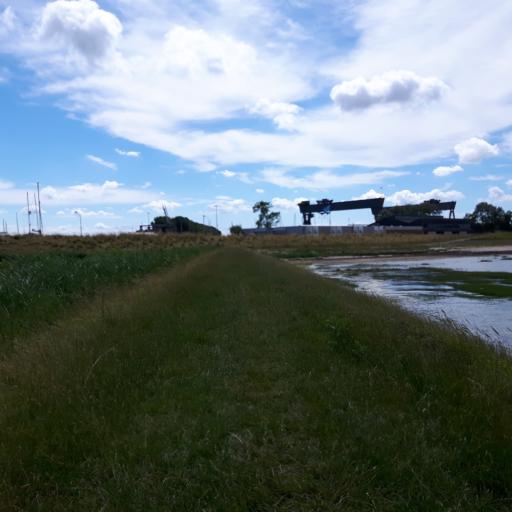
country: NL
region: Zeeland
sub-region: Gemeente Goes
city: Goes
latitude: 51.5755
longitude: 3.8911
